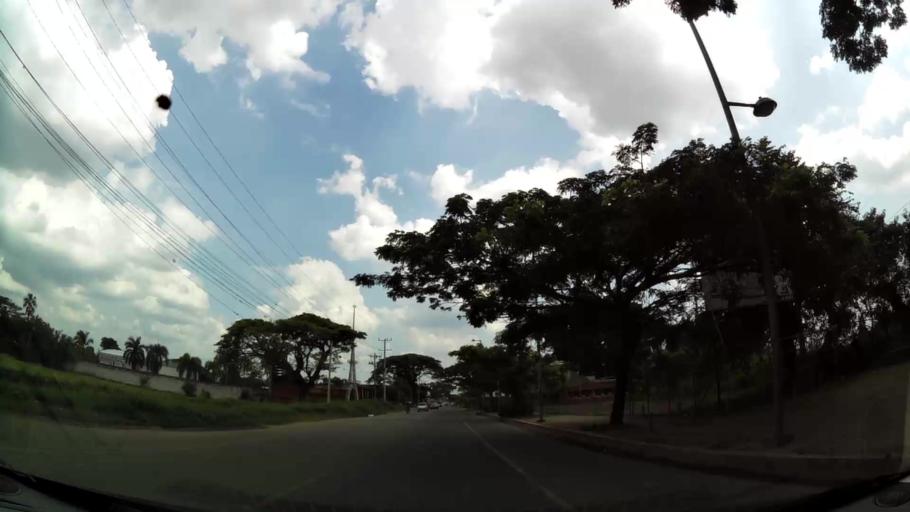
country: CO
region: Valle del Cauca
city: Cali
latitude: 3.4470
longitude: -76.4646
